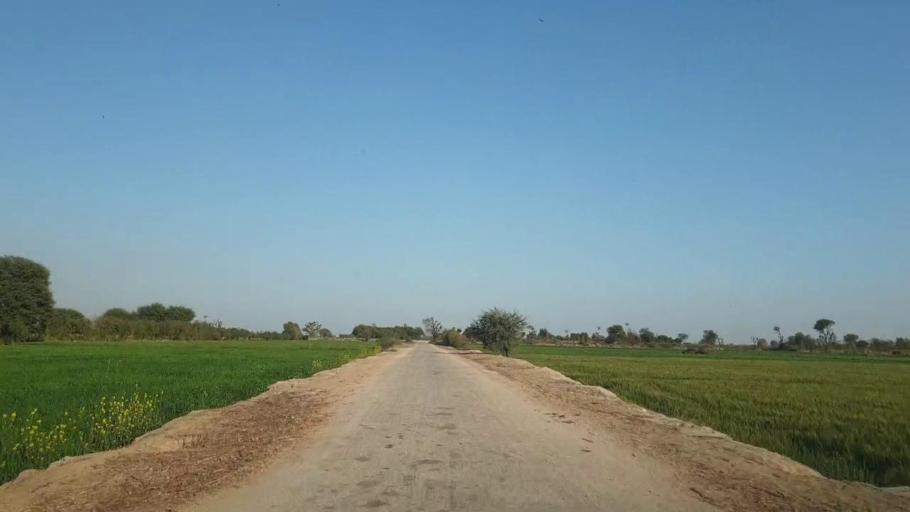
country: PK
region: Sindh
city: Tando Adam
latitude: 25.7006
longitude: 68.6995
